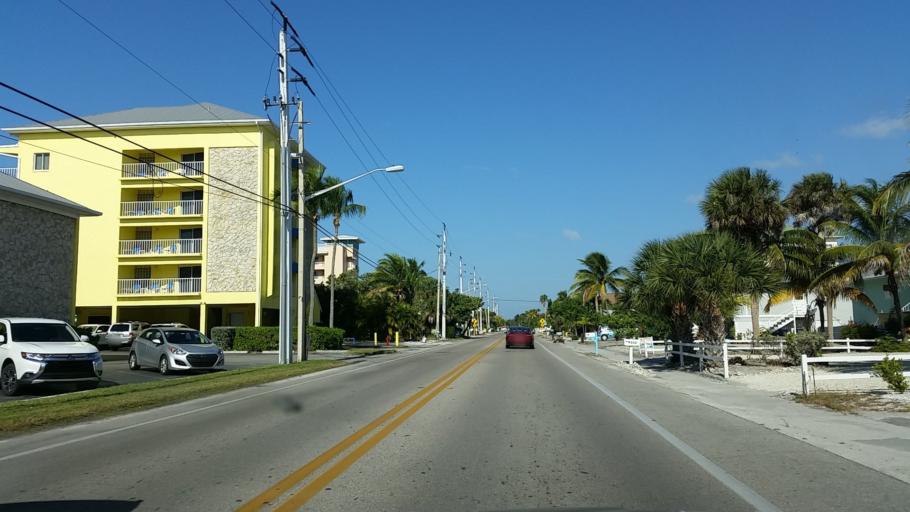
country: US
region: Florida
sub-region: Lee County
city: Fort Myers Beach
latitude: 26.4307
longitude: -81.9136
